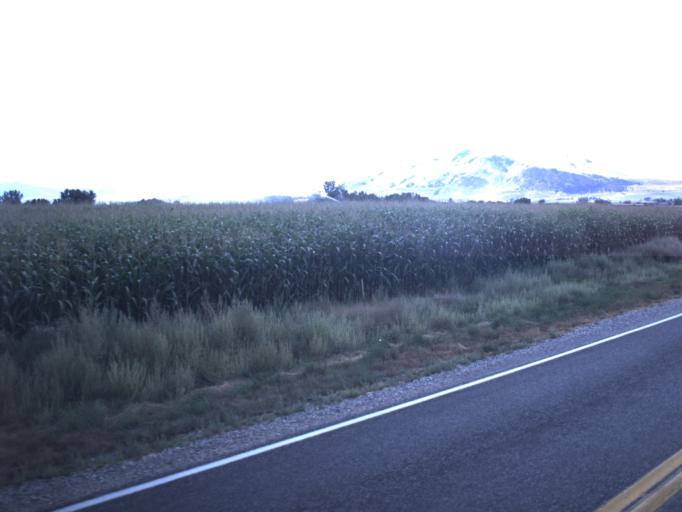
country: US
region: Utah
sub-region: Cache County
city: Lewiston
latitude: 41.9248
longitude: -111.9009
